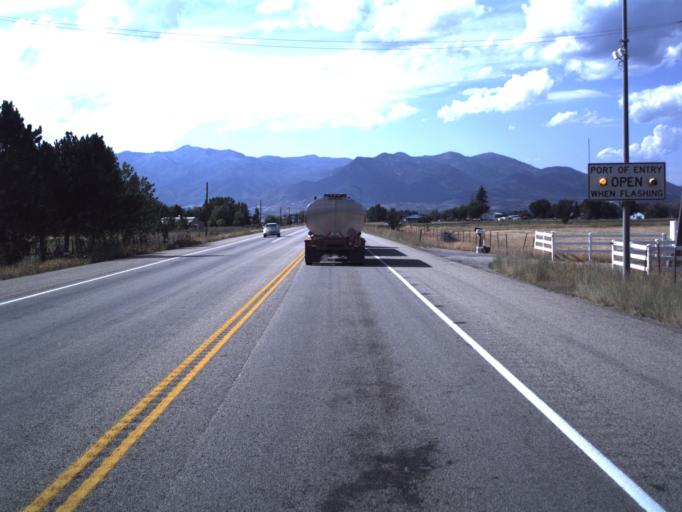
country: US
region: Utah
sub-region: Wasatch County
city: Heber
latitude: 40.4578
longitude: -111.3775
